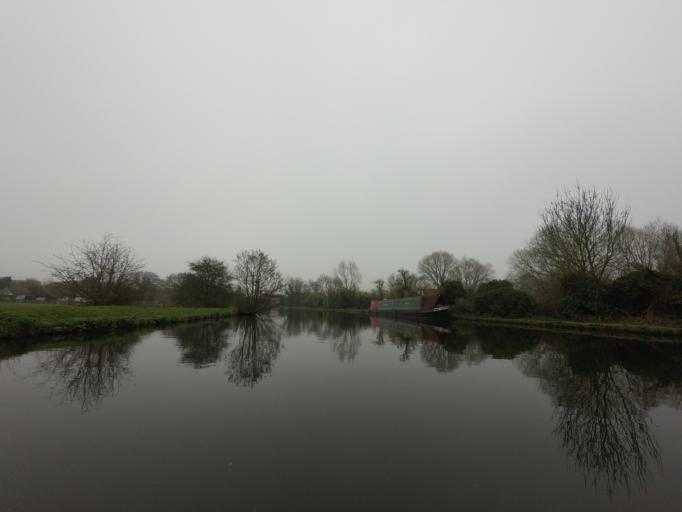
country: GB
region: England
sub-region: Hertfordshire
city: Bovingdon
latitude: 51.7483
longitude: -0.5267
